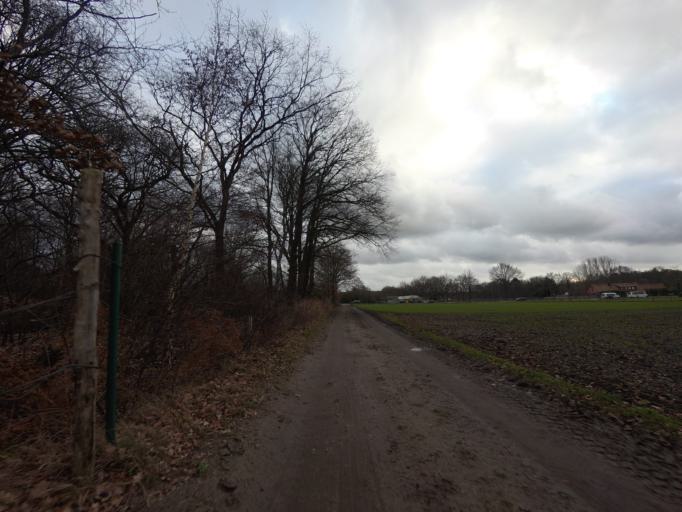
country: BE
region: Flanders
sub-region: Provincie Antwerpen
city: Stabroek
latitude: 51.3437
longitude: 4.3872
